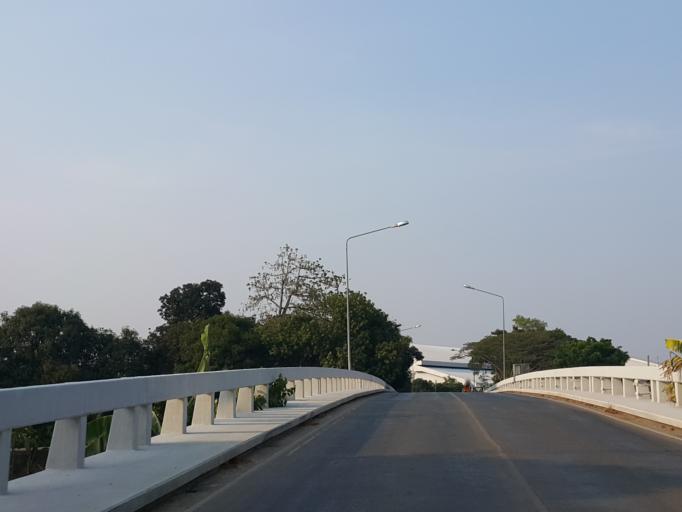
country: TH
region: Chai Nat
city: Sankhaburi
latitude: 15.0635
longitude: 100.1624
